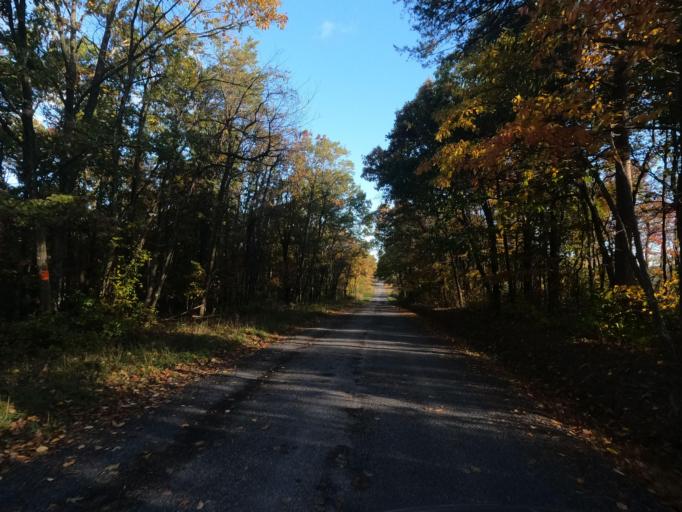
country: US
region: West Virginia
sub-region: Morgan County
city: Berkeley Springs
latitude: 39.6167
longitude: -78.4896
